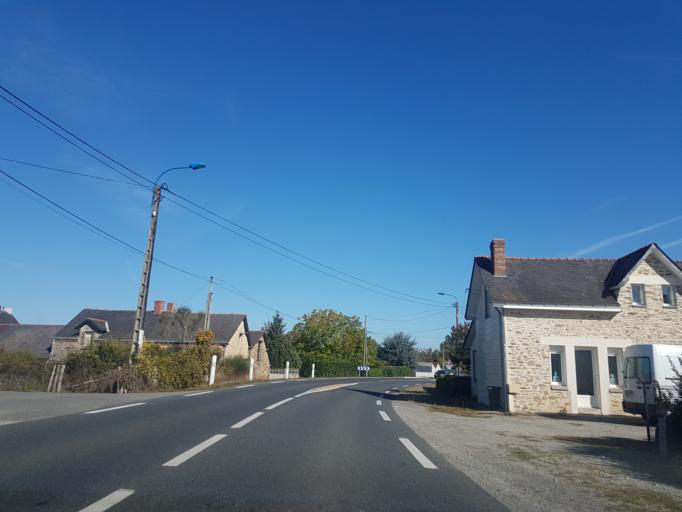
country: FR
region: Pays de la Loire
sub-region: Departement de la Loire-Atlantique
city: Nort-sur-Erdre
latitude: 47.4240
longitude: -1.4827
